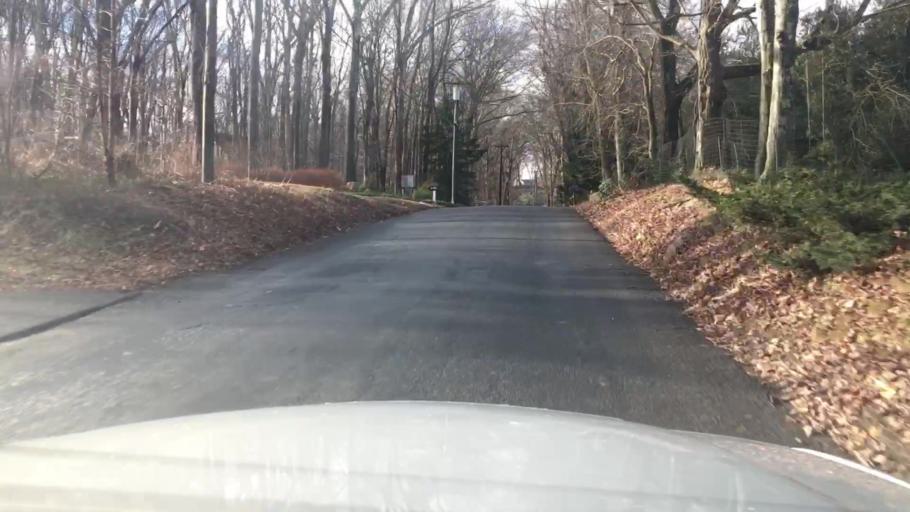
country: US
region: Connecticut
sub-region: Middlesex County
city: Essex Village
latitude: 41.3594
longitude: -72.3975
